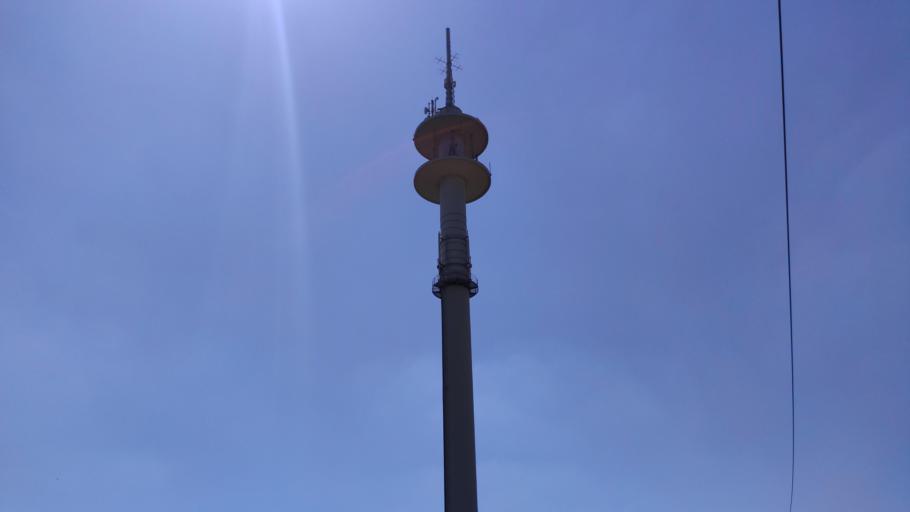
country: DE
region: North Rhine-Westphalia
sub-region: Regierungsbezirk Munster
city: Recklinghausen
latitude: 51.6161
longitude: 7.2254
